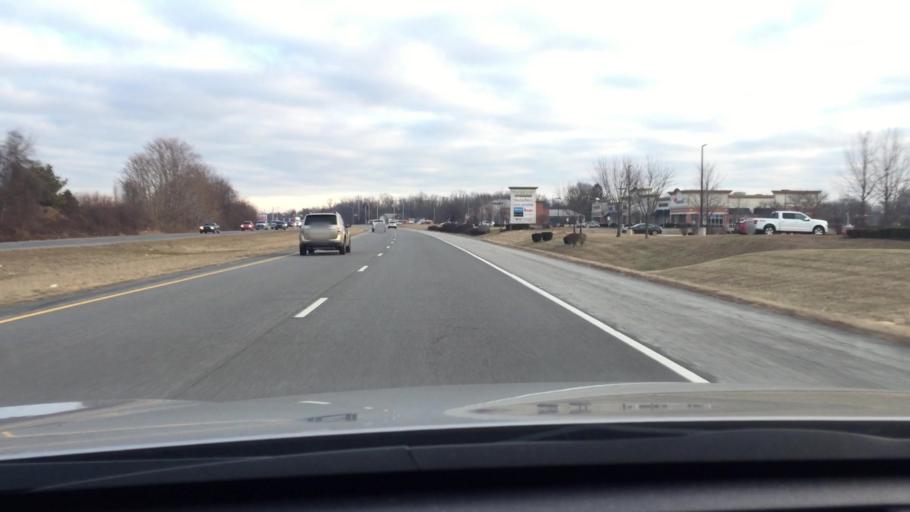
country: US
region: Indiana
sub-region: Hamilton County
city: Noblesville
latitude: 40.0183
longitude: -85.9996
